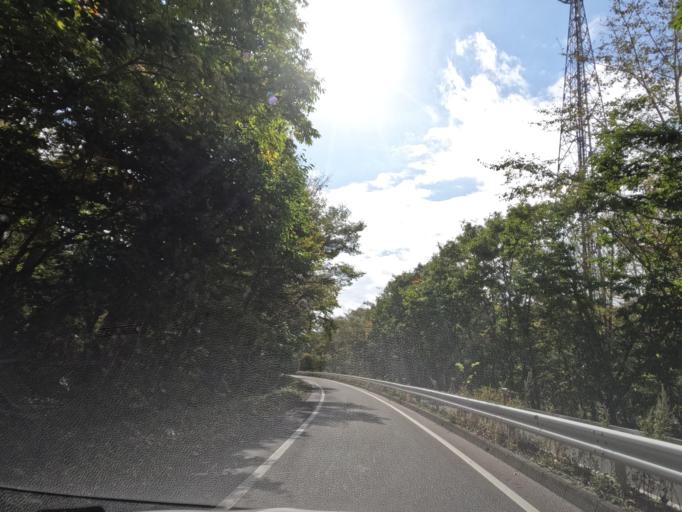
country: JP
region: Hokkaido
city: Chitose
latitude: 42.8010
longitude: 141.5686
